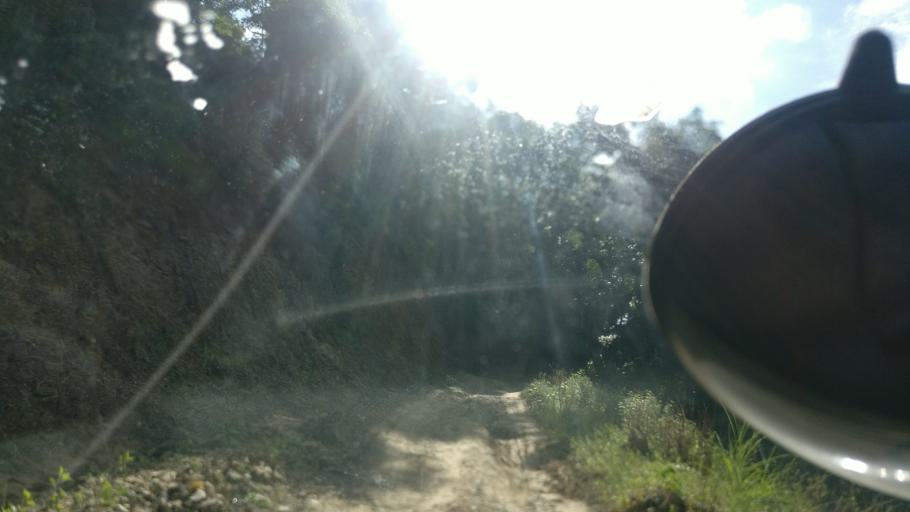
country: NP
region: Western Region
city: Baglung
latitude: 28.1371
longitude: 83.6536
